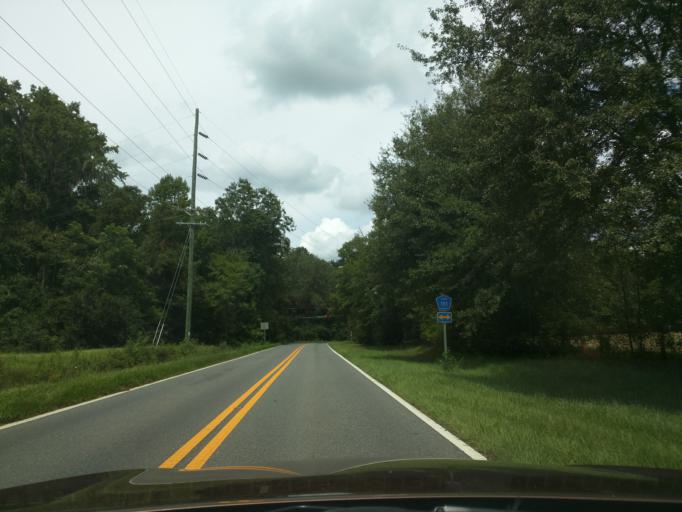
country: US
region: Florida
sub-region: Leon County
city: Tallahassee
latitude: 30.5375
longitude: -84.1752
